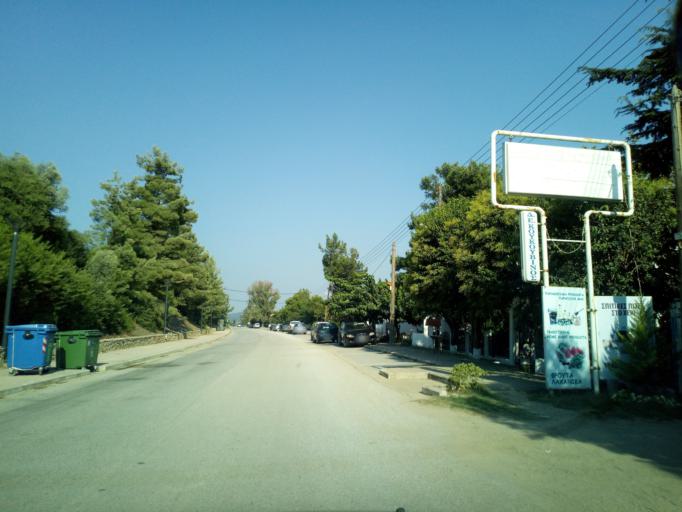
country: GR
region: Central Macedonia
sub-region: Nomos Chalkidikis
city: Ormylia
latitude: 40.2589
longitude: 23.4998
